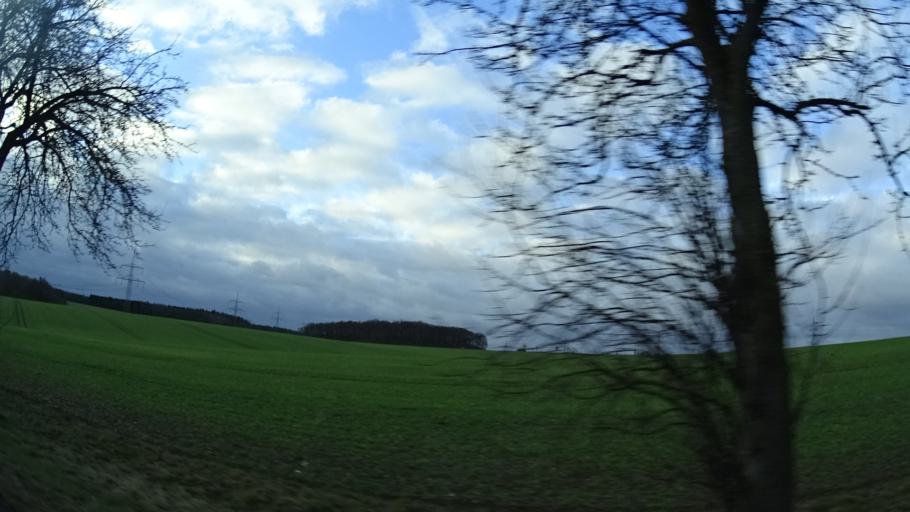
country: DE
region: Thuringia
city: Auma
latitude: 50.6821
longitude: 11.9180
